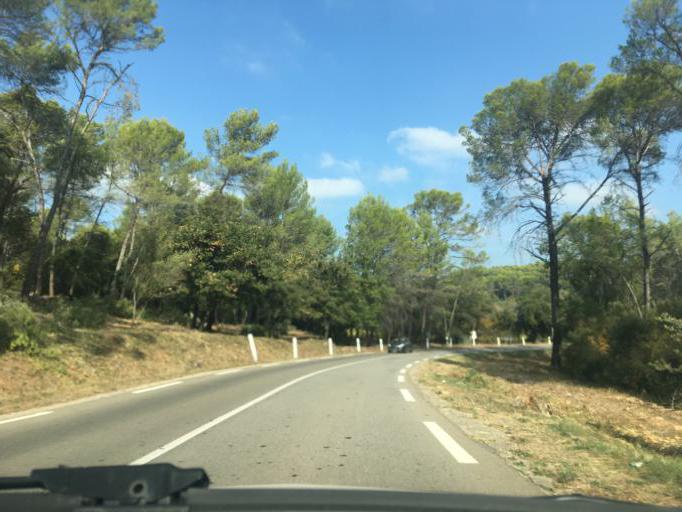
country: FR
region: Provence-Alpes-Cote d'Azur
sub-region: Departement du Var
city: Flayosc
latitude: 43.5052
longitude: 6.4209
